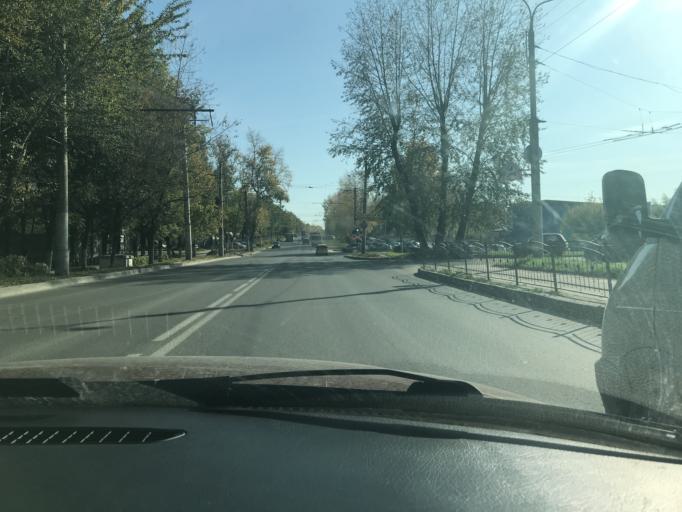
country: RU
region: Kaluga
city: Kaluga
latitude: 54.5509
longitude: 36.2680
